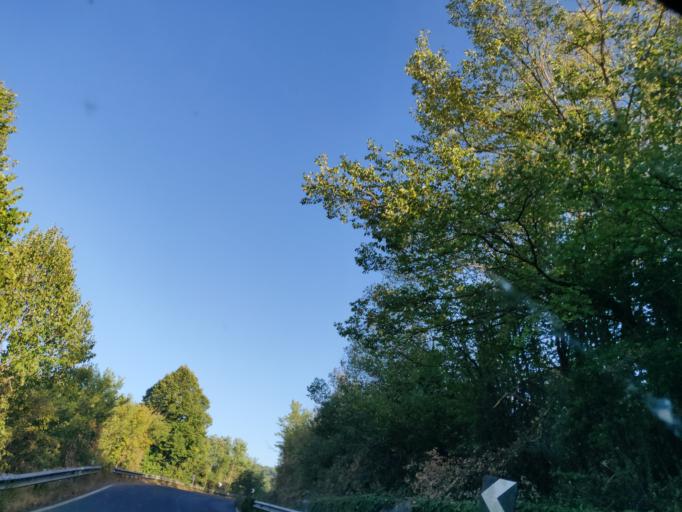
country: IT
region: Latium
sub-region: Provincia di Viterbo
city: Acquapendente
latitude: 42.7580
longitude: 11.8647
